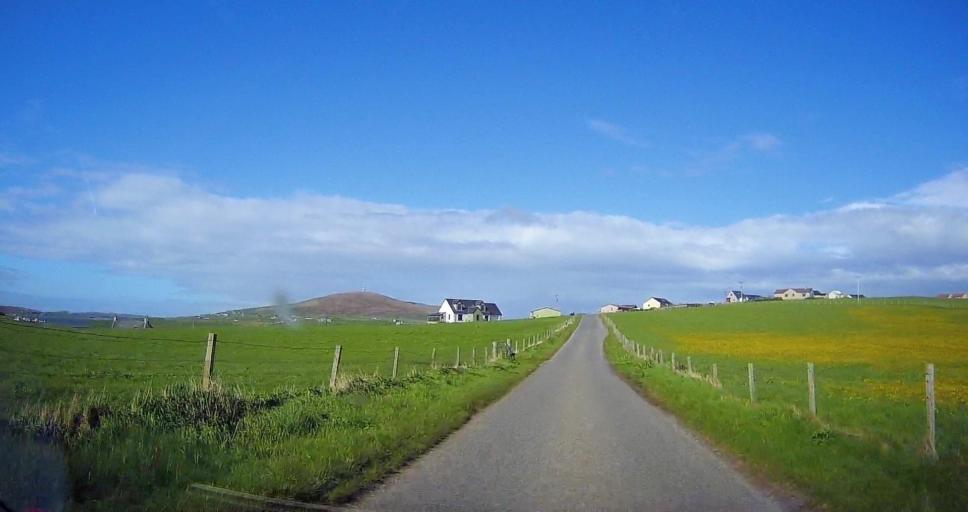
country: GB
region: Scotland
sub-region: Shetland Islands
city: Sandwick
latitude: 59.9143
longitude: -1.3232
